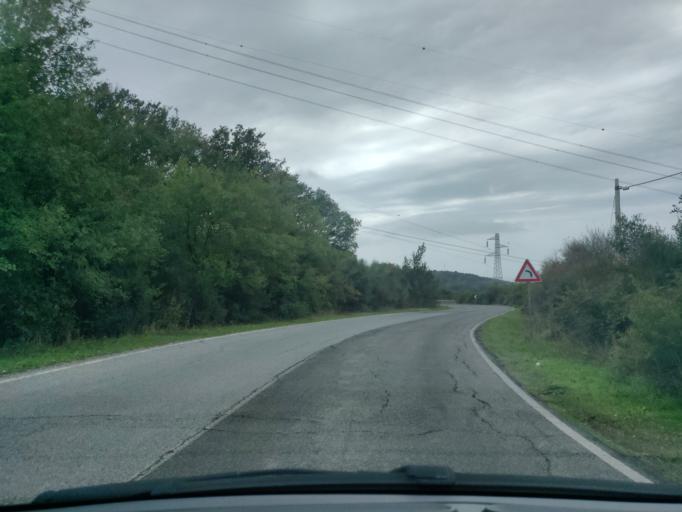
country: IT
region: Latium
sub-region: Citta metropolitana di Roma Capitale
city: Allumiere
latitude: 42.1241
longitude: 11.8638
